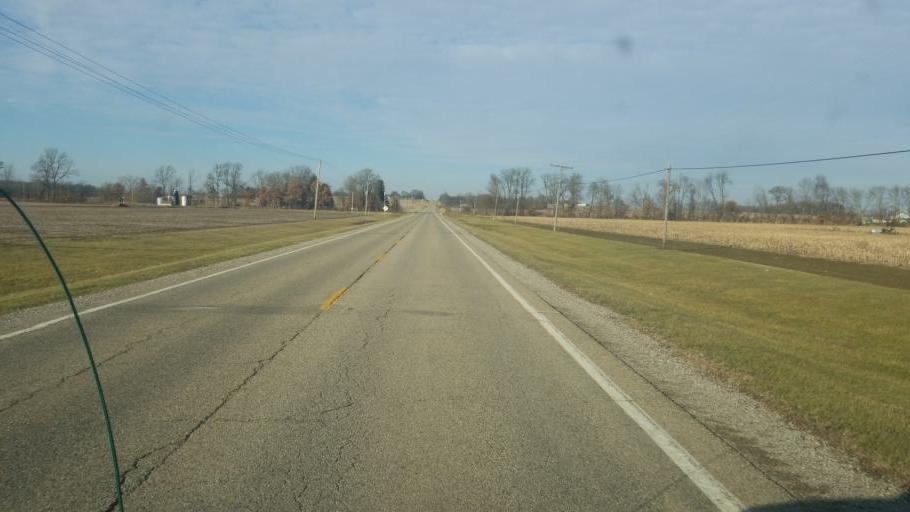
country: US
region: Illinois
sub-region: Lawrence County
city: Lawrenceville
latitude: 38.6440
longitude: -87.6943
